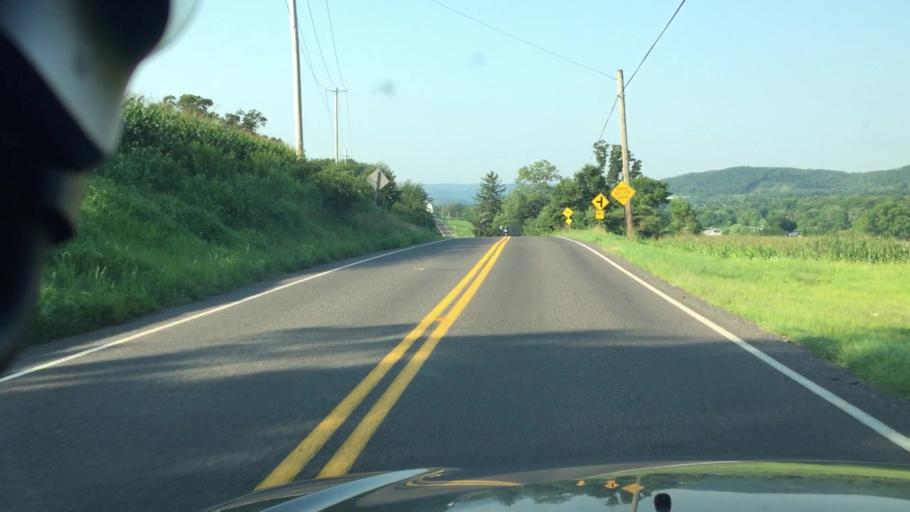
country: US
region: Pennsylvania
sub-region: Columbia County
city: Mifflinville
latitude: 40.9985
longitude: -76.3255
